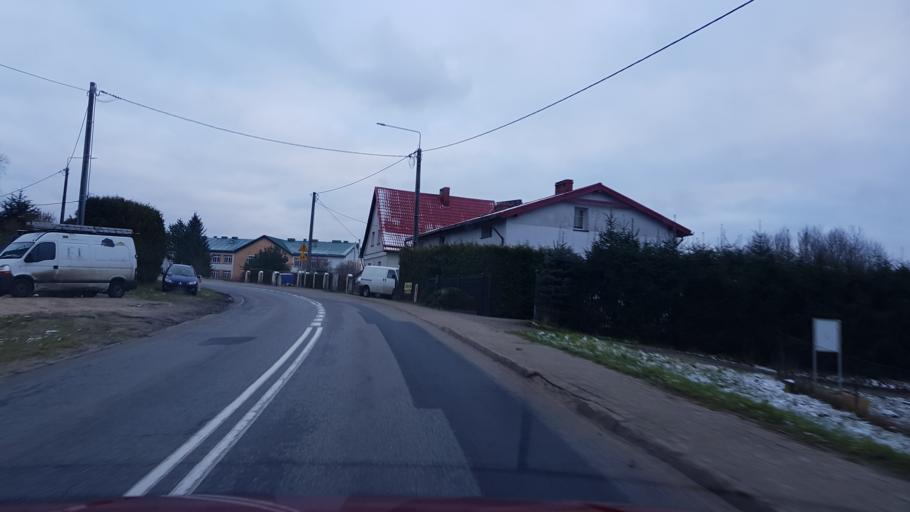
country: PL
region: Pomeranian Voivodeship
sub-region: Powiat bytowski
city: Miastko
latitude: 54.0214
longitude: 16.9496
